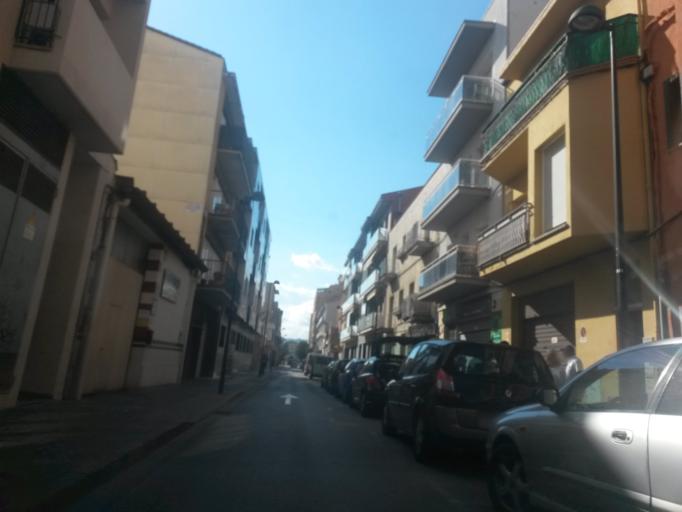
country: ES
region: Catalonia
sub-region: Provincia de Girona
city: Girona
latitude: 41.9696
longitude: 2.8165
